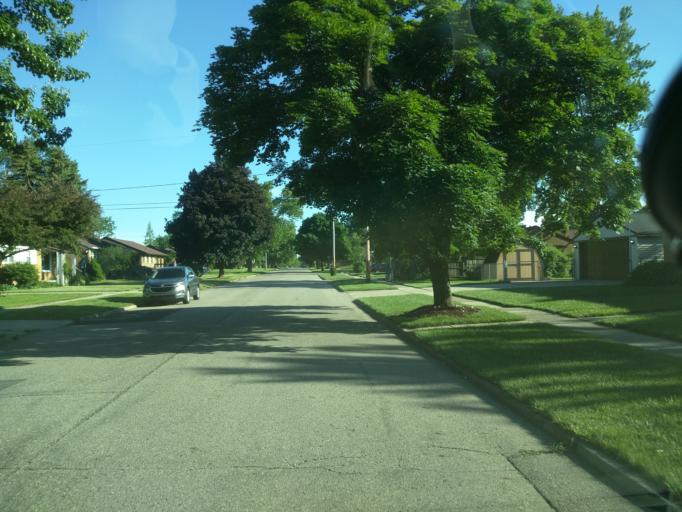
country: US
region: Michigan
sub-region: Ingham County
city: Edgemont Park
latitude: 42.7474
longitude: -84.5963
